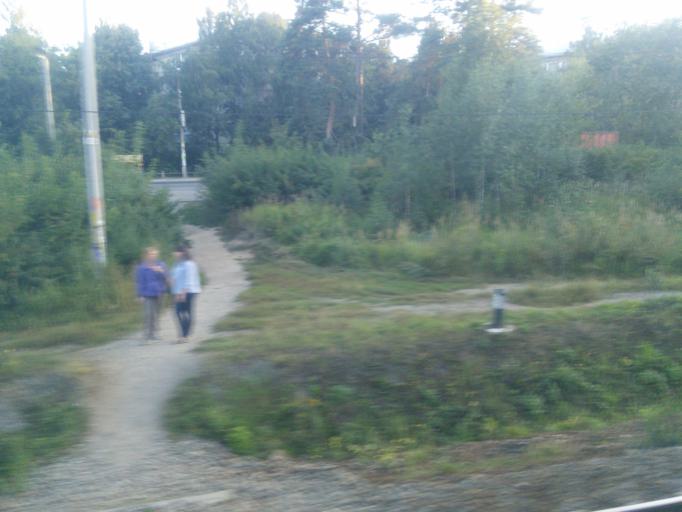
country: RU
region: Moskovskaya
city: Kupavna
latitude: 55.7460
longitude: 38.1471
